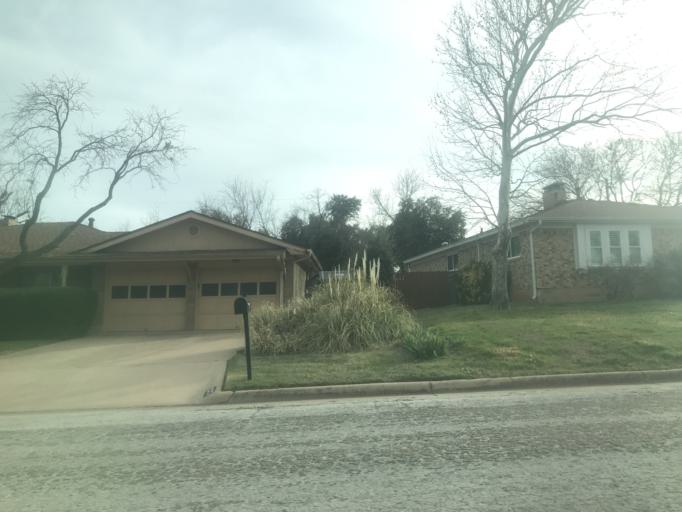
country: US
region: Texas
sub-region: Taylor County
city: Abilene
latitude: 32.3960
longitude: -99.7561
